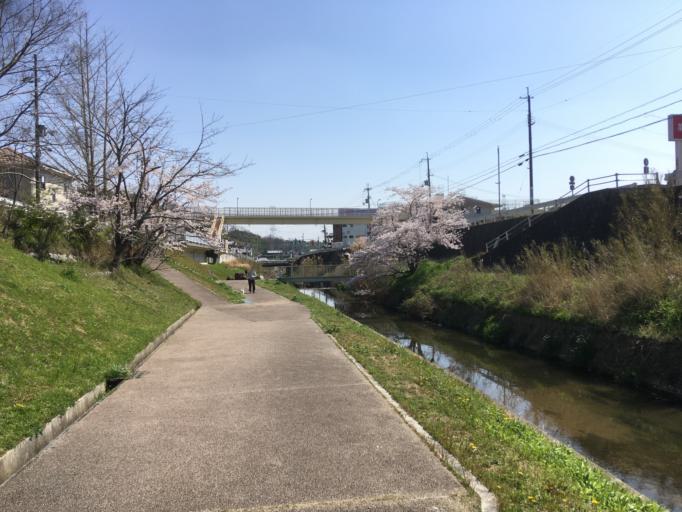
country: JP
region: Nara
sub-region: Ikoma-shi
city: Ikoma
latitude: 34.7422
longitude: 135.7217
